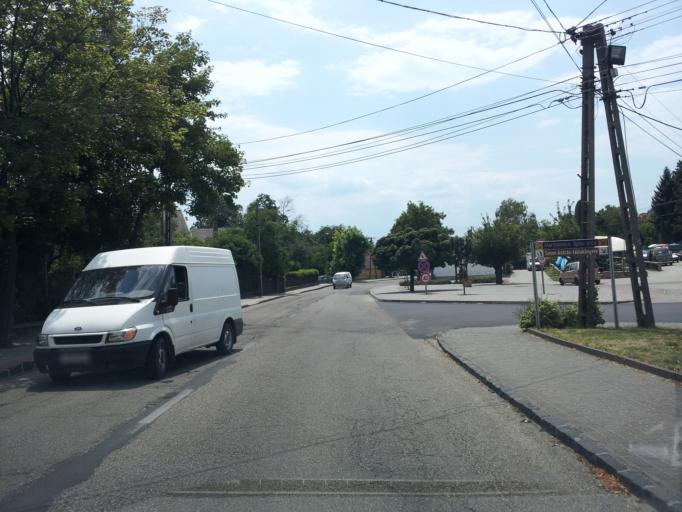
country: HU
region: Veszprem
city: Balatonalmadi
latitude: 47.0342
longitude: 18.0141
